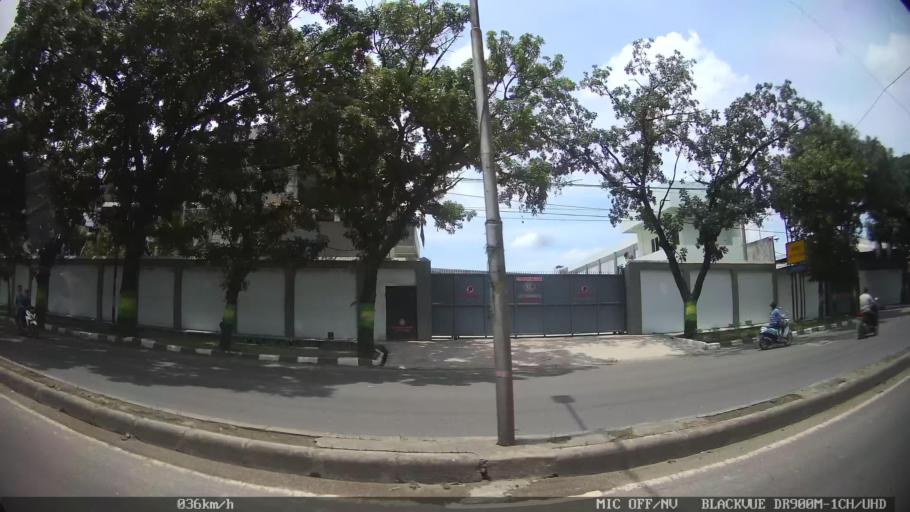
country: ID
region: North Sumatra
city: Labuhan Deli
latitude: 3.7066
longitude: 98.6796
